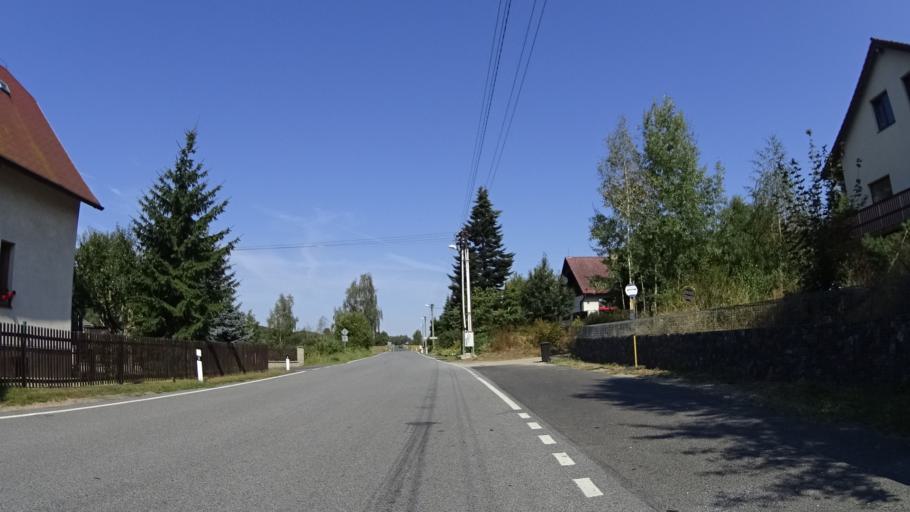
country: CZ
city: Chrastava
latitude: 50.7955
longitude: 14.9896
